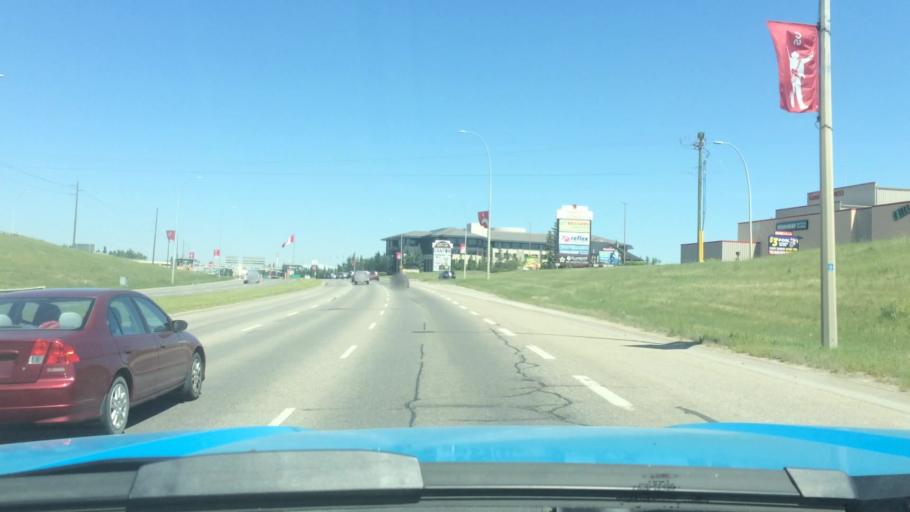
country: CA
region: Alberta
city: Calgary
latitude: 50.9318
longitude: -114.0685
